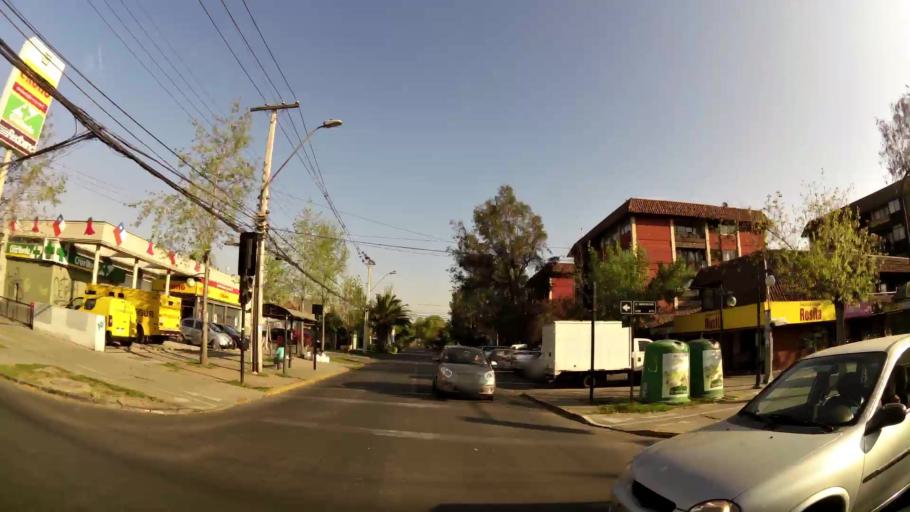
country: CL
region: Santiago Metropolitan
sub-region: Provincia de Santiago
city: Villa Presidente Frei, Nunoa, Santiago, Chile
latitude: -33.4483
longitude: -70.5808
